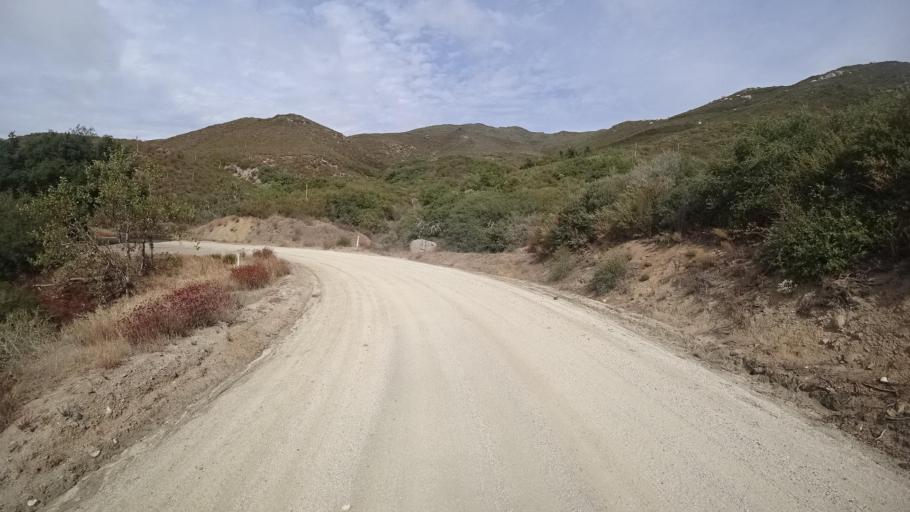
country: US
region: California
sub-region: San Diego County
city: Descanso
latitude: 32.9211
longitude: -116.6293
